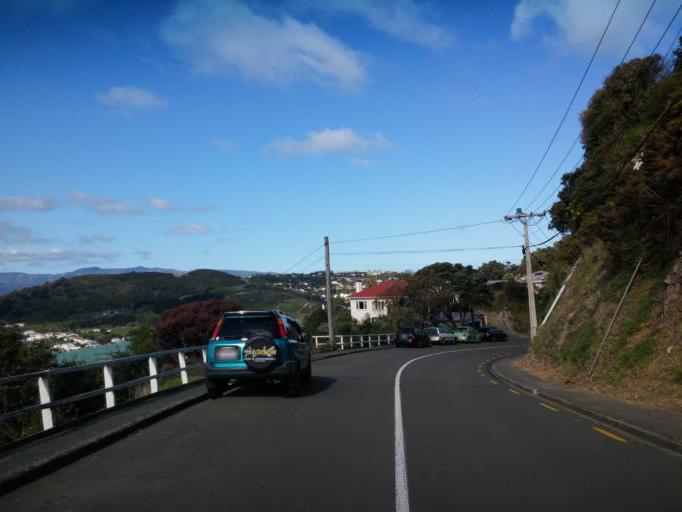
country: NZ
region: Wellington
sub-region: Wellington City
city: Brooklyn
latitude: -41.3197
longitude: 174.7656
